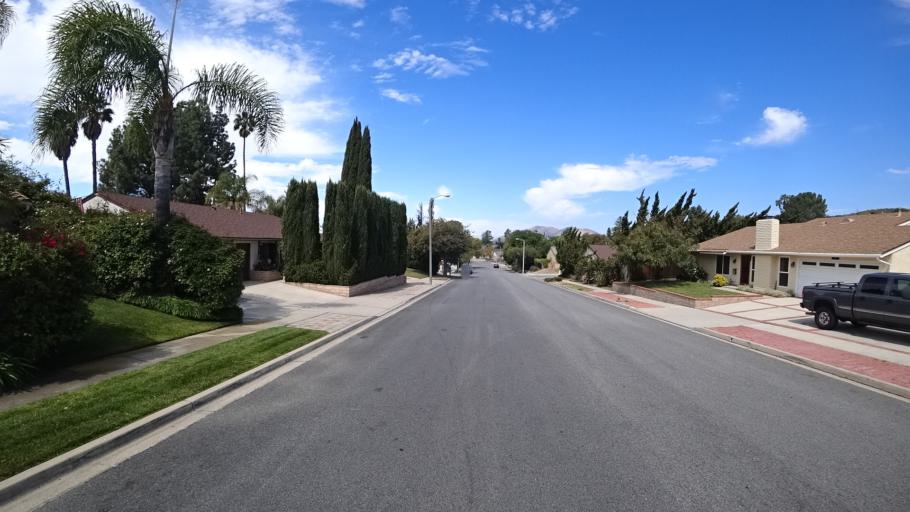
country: US
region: California
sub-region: Ventura County
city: Casa Conejo
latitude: 34.1658
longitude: -118.9384
